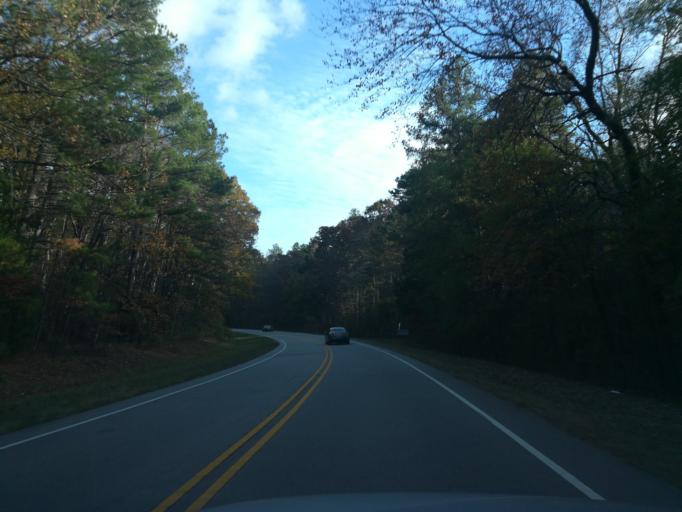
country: US
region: North Carolina
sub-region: Durham County
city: Durham
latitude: 36.0220
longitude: -78.9879
